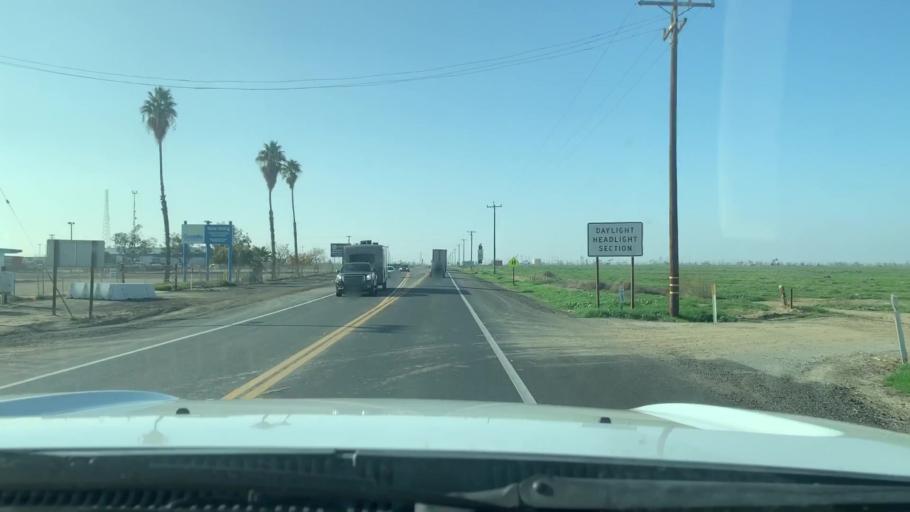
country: US
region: California
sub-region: Kern County
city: Lost Hills
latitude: 35.6160
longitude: -119.7073
